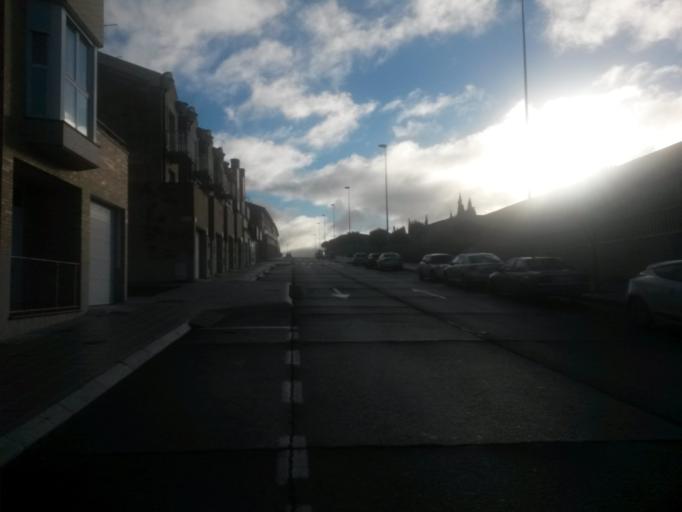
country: ES
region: Castille and Leon
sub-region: Provincia de Salamanca
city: Salamanca
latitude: 40.9790
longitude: -5.6480
